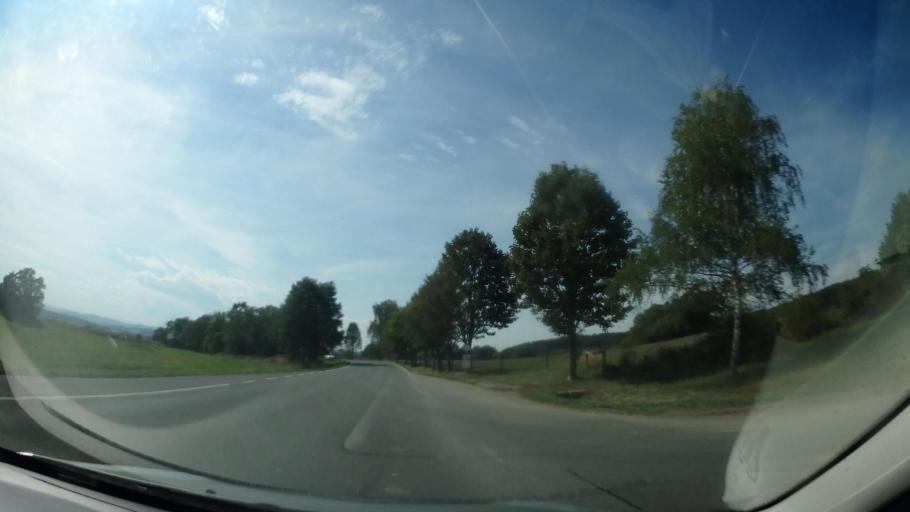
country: CZ
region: Jihocesky
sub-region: Okres Pisek
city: Pisek
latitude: 49.3060
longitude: 14.0733
